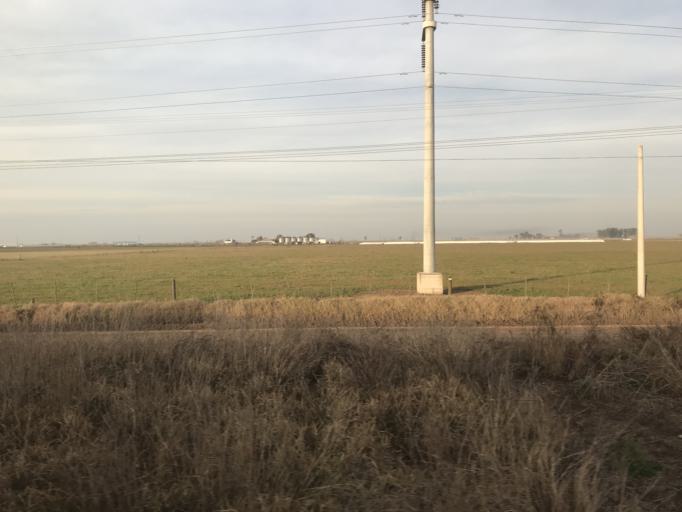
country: AR
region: Cordoba
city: Marcos Juarez
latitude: -32.6826
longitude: -62.1986
